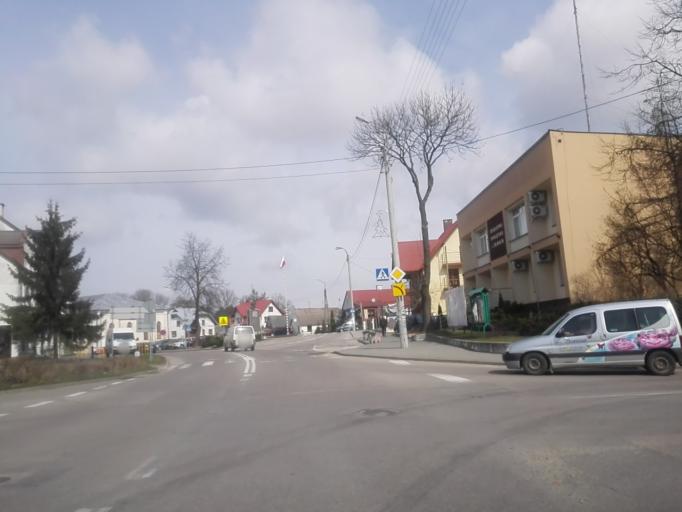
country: PL
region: Podlasie
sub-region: Powiat sejnenski
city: Sejny
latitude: 54.1044
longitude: 23.3511
